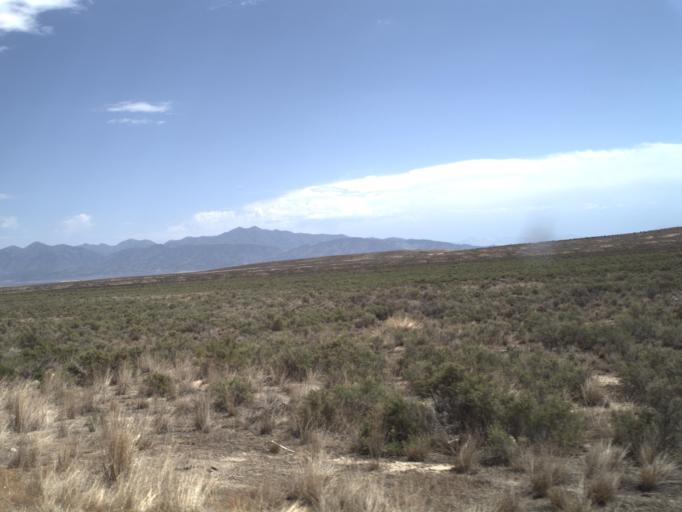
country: US
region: Utah
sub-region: Tooele County
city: Tooele
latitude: 40.1378
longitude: -112.4308
